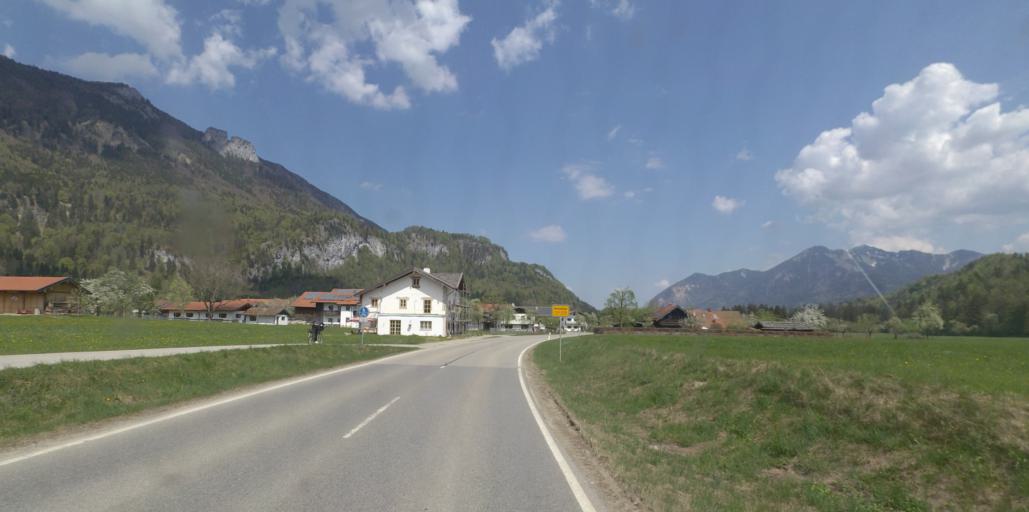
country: DE
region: Bavaria
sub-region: Upper Bavaria
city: Schleching
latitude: 47.7276
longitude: 12.4096
